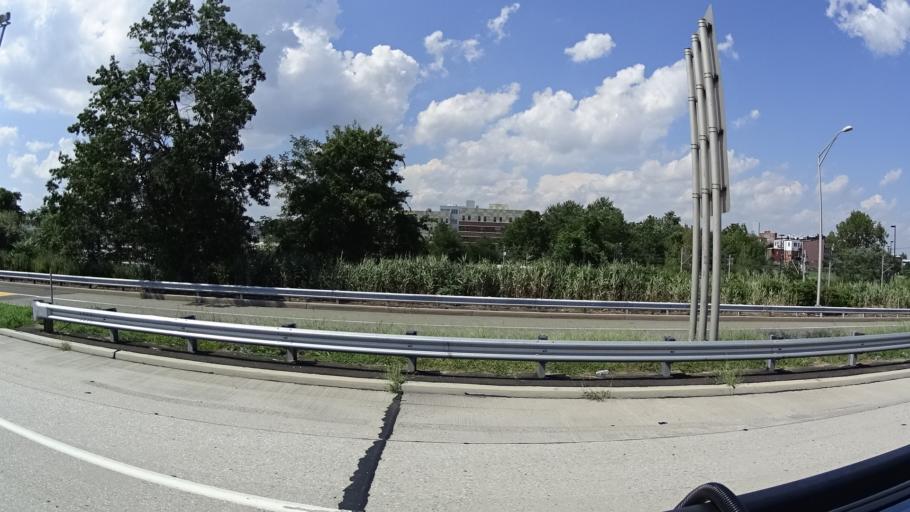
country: US
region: New Jersey
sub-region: Hudson County
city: Jersey City
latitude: 40.7073
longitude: -74.0602
